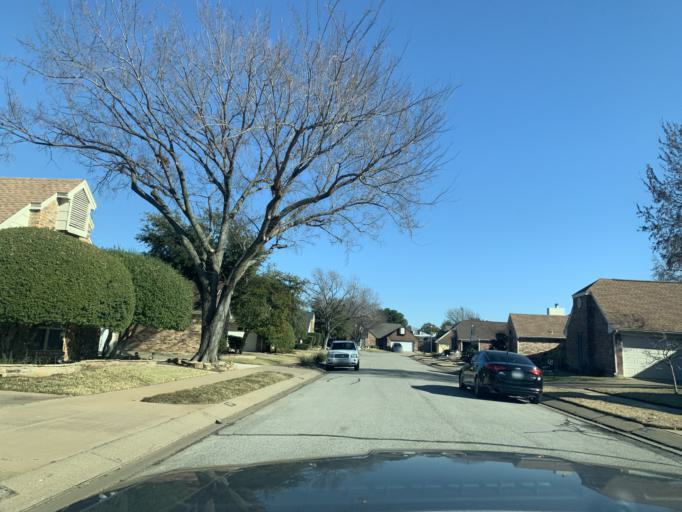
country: US
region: Texas
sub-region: Tarrant County
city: Bedford
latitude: 32.8316
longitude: -97.1388
